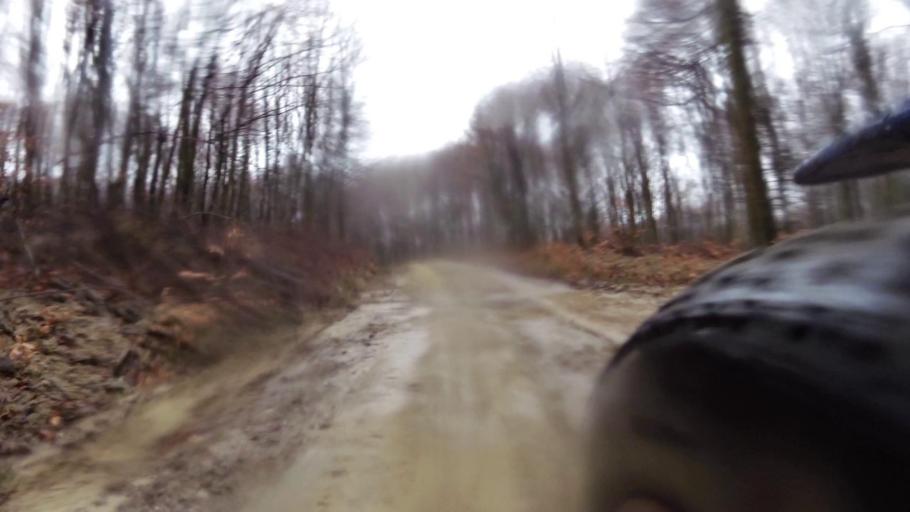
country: PL
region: West Pomeranian Voivodeship
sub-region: Powiat drawski
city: Czaplinek
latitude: 53.6076
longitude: 16.2945
